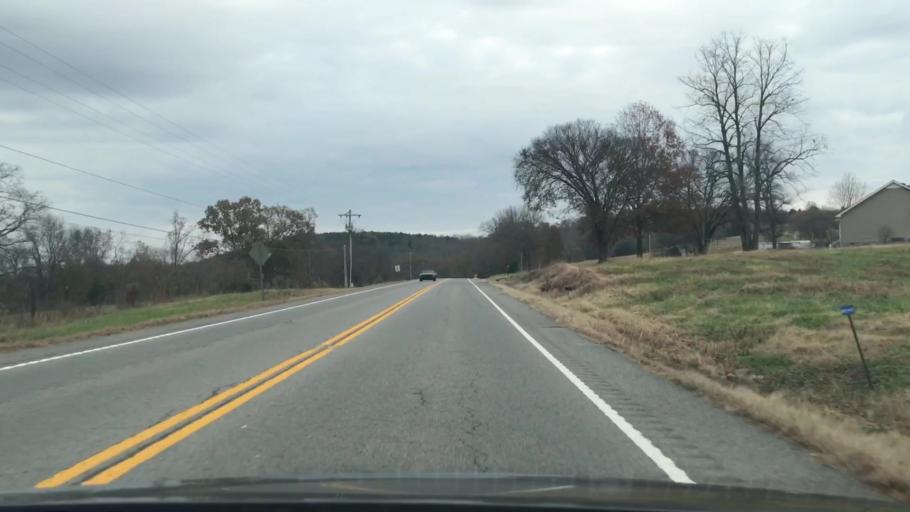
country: US
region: Tennessee
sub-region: Trousdale County
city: Hartsville
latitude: 36.3957
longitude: -86.1094
